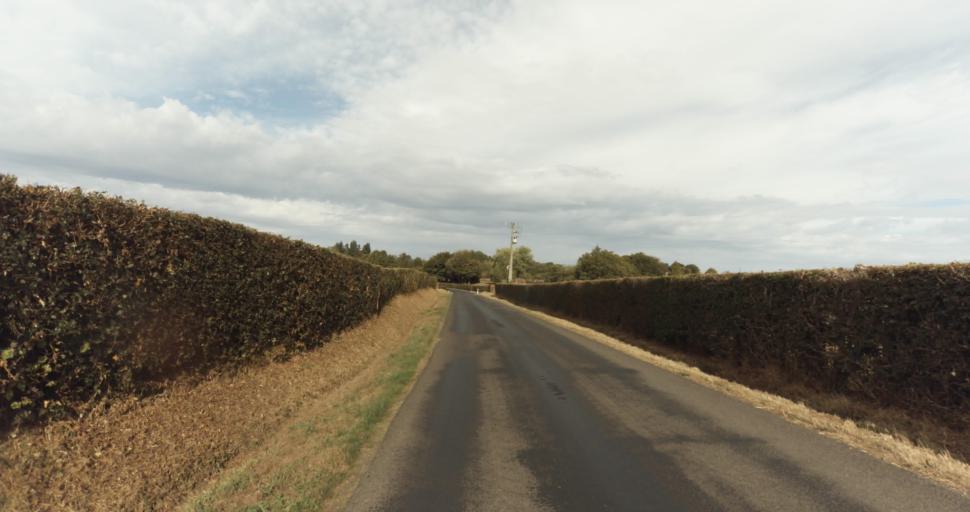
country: FR
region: Lower Normandy
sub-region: Departement de l'Orne
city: Vimoutiers
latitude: 48.9316
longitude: 0.2396
